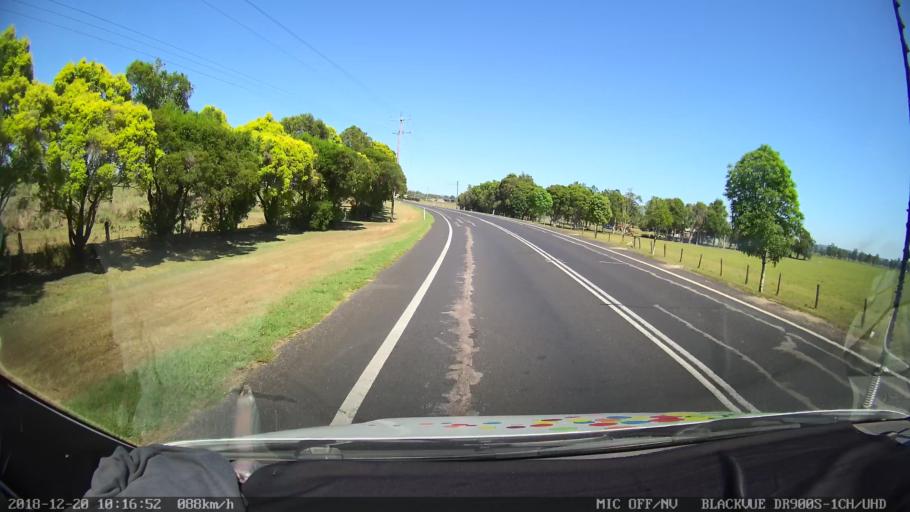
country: AU
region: New South Wales
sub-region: Richmond Valley
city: Casino
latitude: -28.8607
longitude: 153.0782
